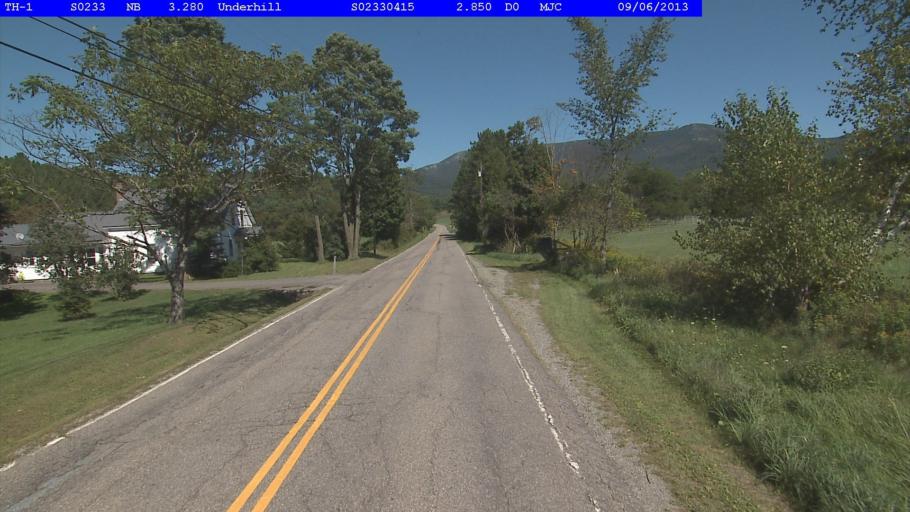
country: US
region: Vermont
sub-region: Chittenden County
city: Jericho
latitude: 44.5110
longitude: -72.8915
